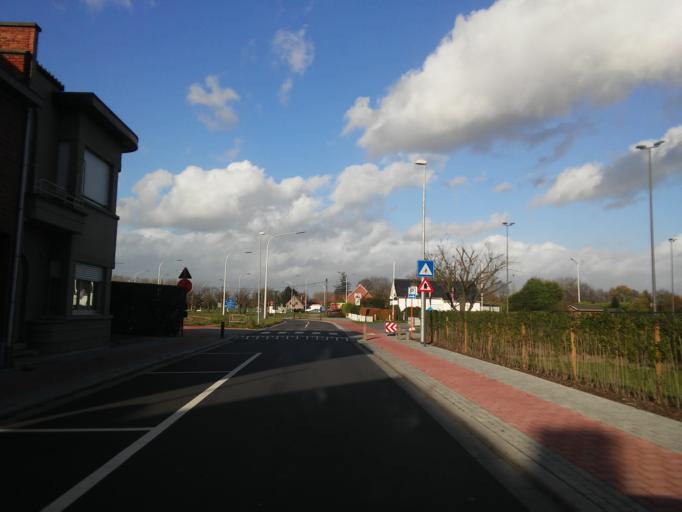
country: BE
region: Flanders
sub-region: Provincie Antwerpen
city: Puurs
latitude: 51.0767
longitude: 4.2963
